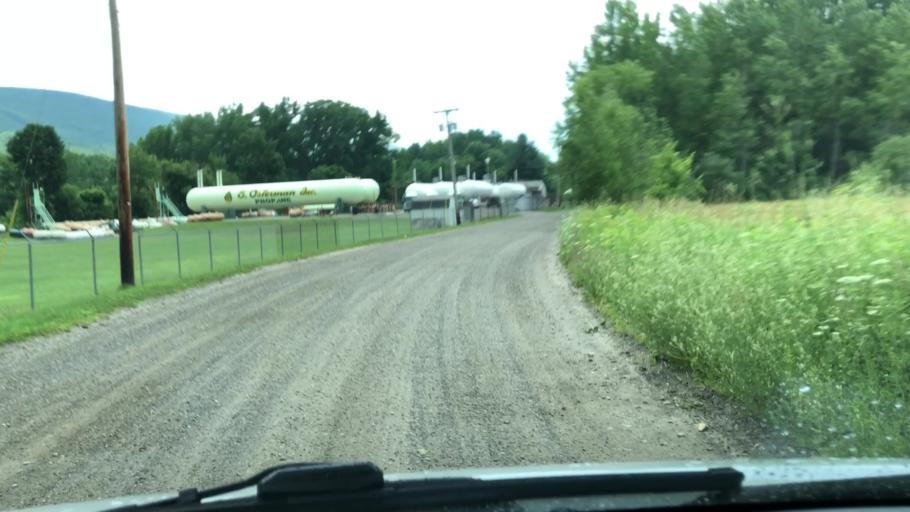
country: US
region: Massachusetts
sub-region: Berkshire County
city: North Adams
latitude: 42.6690
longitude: -73.1049
